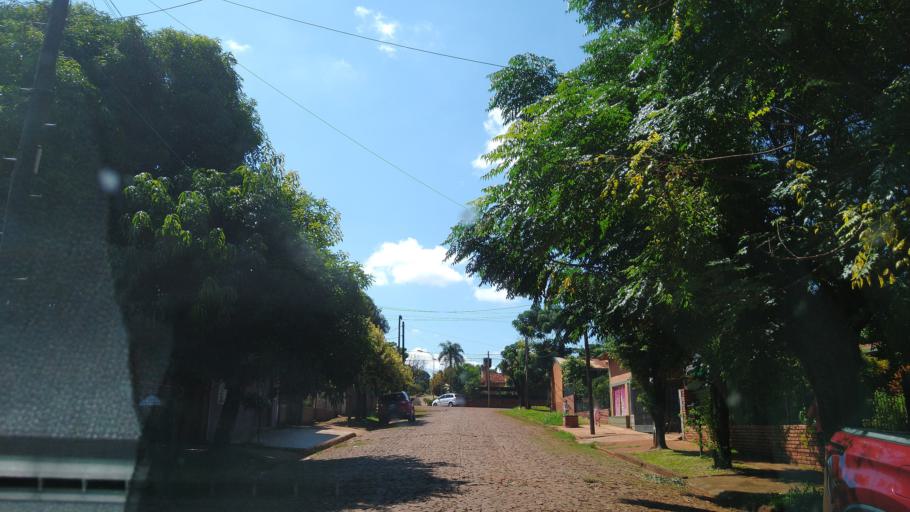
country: AR
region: Misiones
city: Puerto Libertad
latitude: -25.9680
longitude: -54.5614
